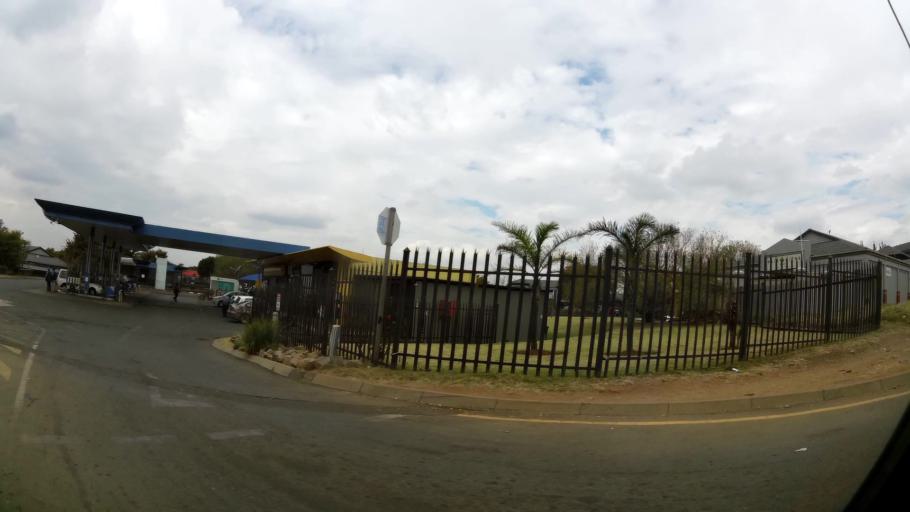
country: ZA
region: Gauteng
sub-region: West Rand District Municipality
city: Muldersdriseloop
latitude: -26.0904
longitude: 27.8703
